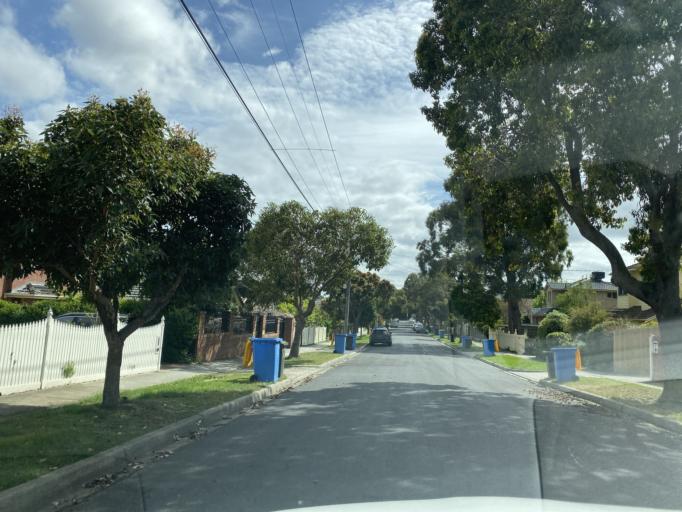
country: AU
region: Victoria
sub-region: Boroondara
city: Ashburton
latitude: -37.8510
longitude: 145.0838
